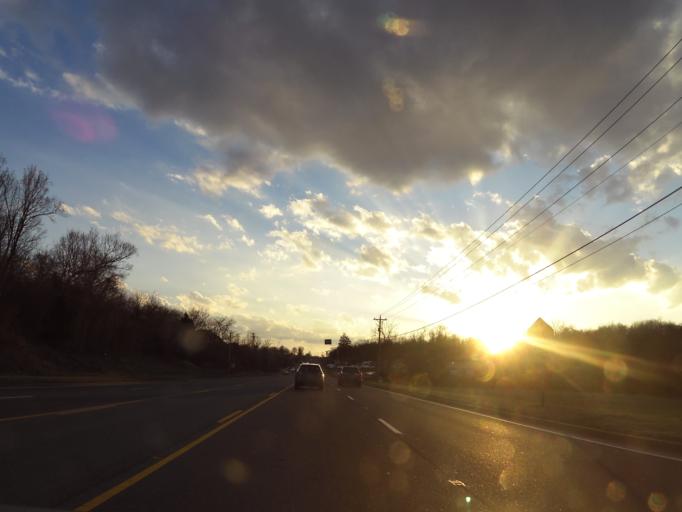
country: US
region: Tennessee
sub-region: Wilson County
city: Green Hill
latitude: 36.2288
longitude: -86.5348
